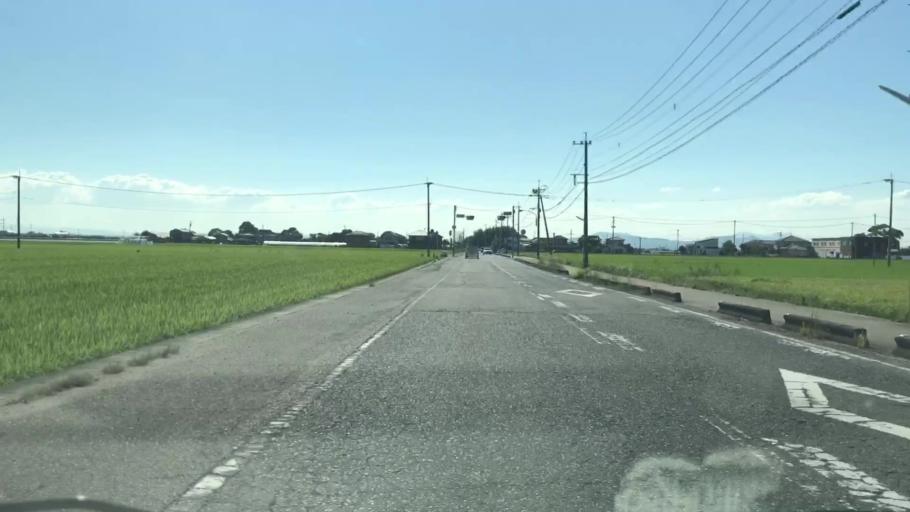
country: JP
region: Saga Prefecture
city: Okawa
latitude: 33.2202
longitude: 130.3456
